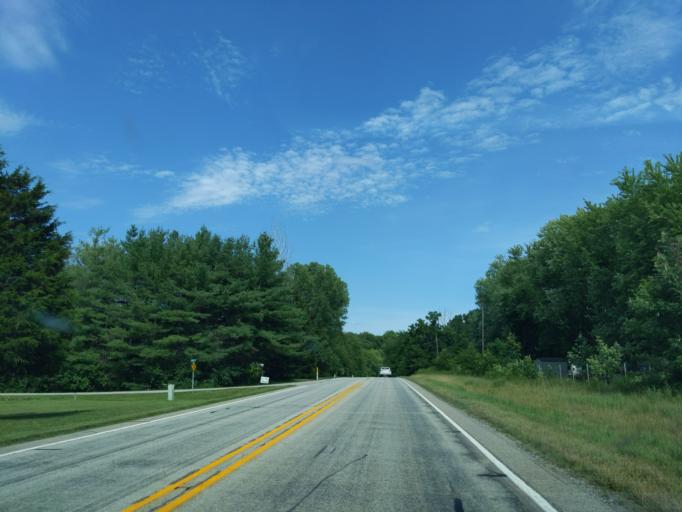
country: US
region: Indiana
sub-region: Ripley County
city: Sunman
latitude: 39.2772
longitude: -85.1183
